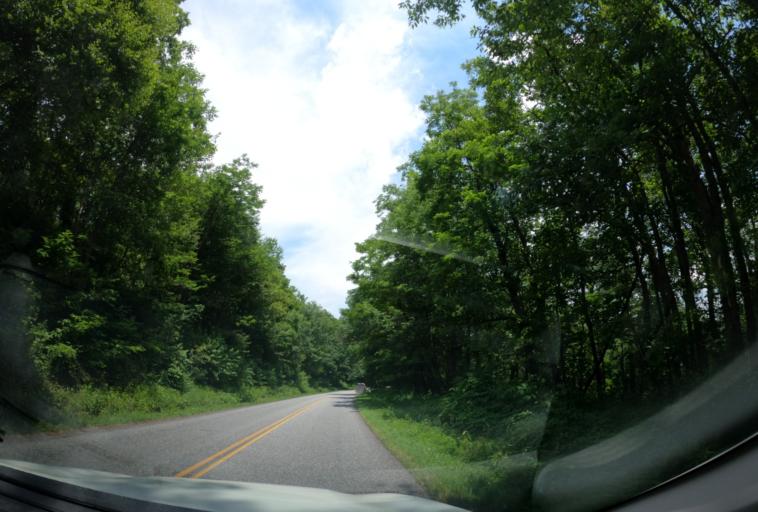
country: US
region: North Carolina
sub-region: Haywood County
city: Canton
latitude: 35.4301
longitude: -82.7380
